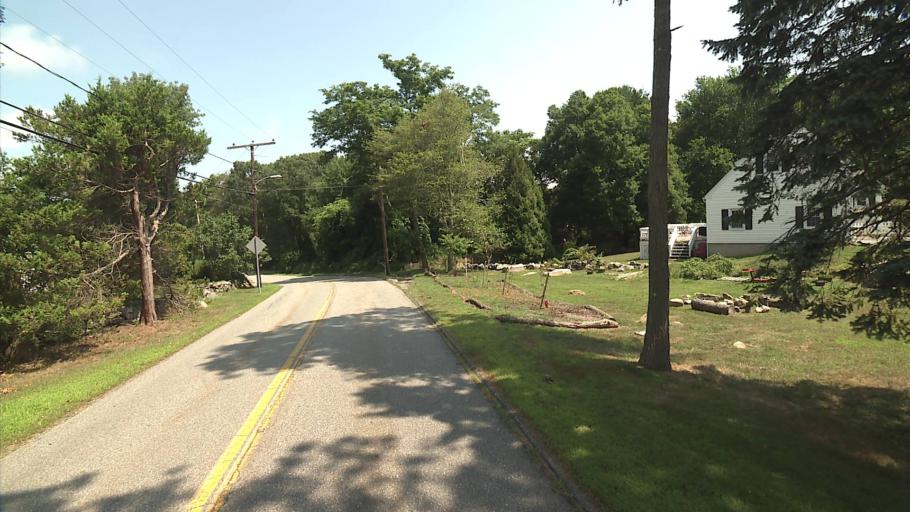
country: US
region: Connecticut
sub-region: New London County
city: Central Waterford
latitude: 41.3172
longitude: -72.1063
